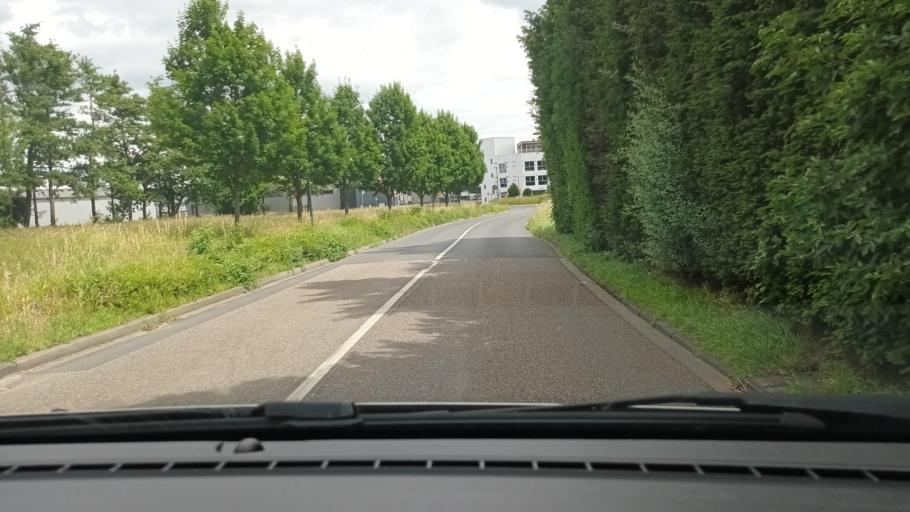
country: DE
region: North Rhine-Westphalia
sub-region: Regierungsbezirk Koln
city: Hurth
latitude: 50.8690
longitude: 6.8953
